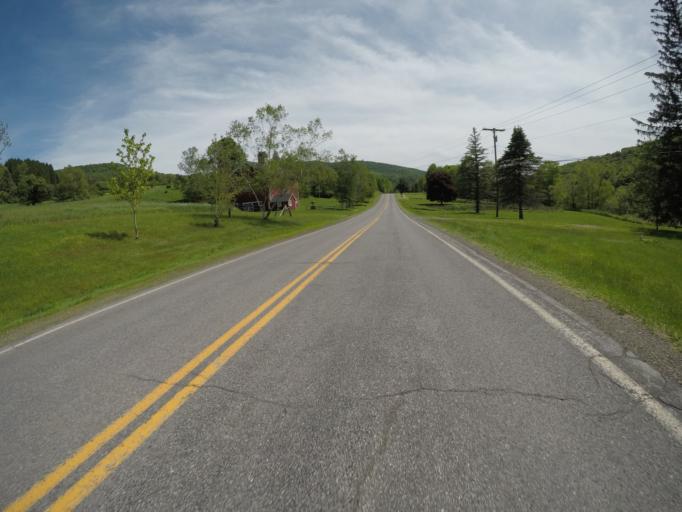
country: US
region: New York
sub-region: Delaware County
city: Delhi
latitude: 42.1775
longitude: -74.7899
